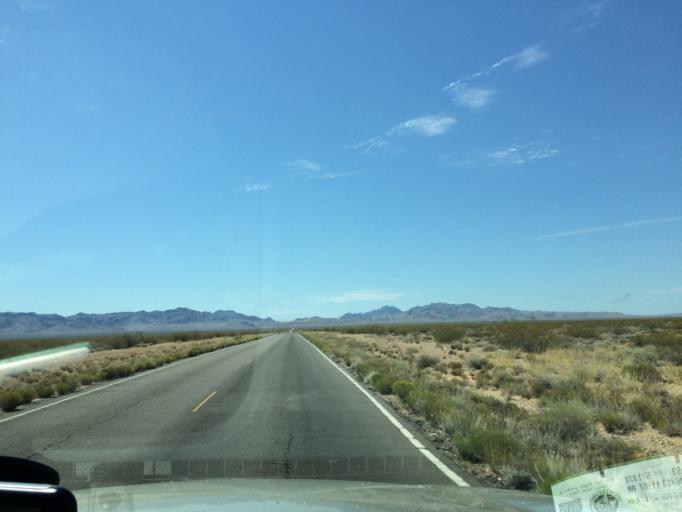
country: US
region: Nevada
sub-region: Clark County
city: Moapa Town
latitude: 36.4823
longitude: -114.7470
